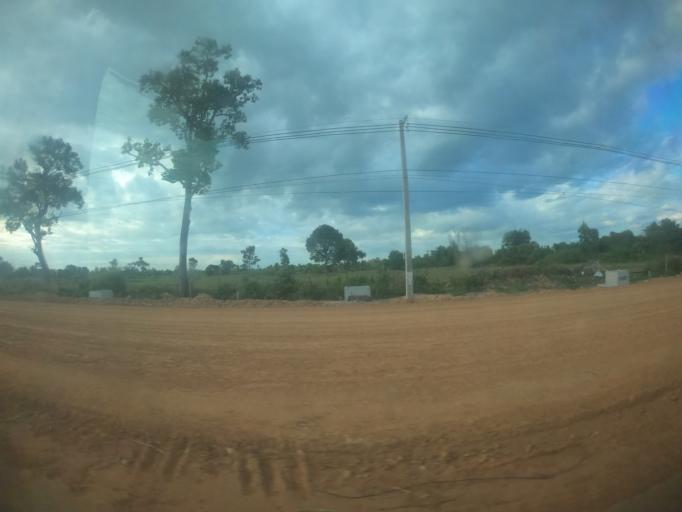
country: TH
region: Surin
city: Kap Choeng
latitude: 14.4566
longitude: 103.6763
